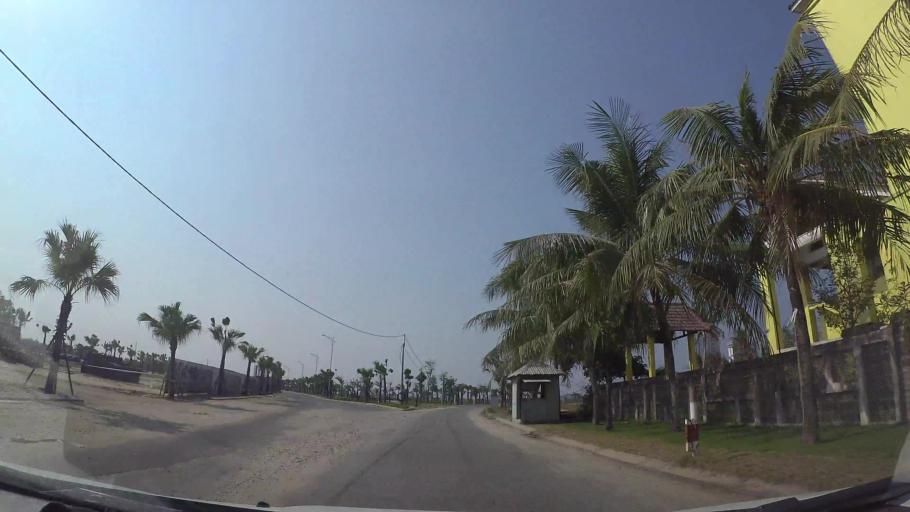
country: VN
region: Da Nang
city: Ngu Hanh Son
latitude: 15.9574
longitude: 108.2787
